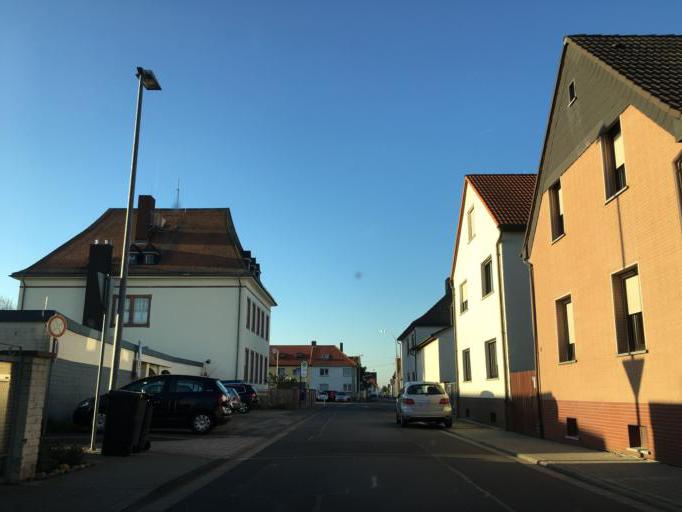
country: DE
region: Hesse
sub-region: Regierungsbezirk Darmstadt
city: Rodgau
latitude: 50.0076
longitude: 8.8862
